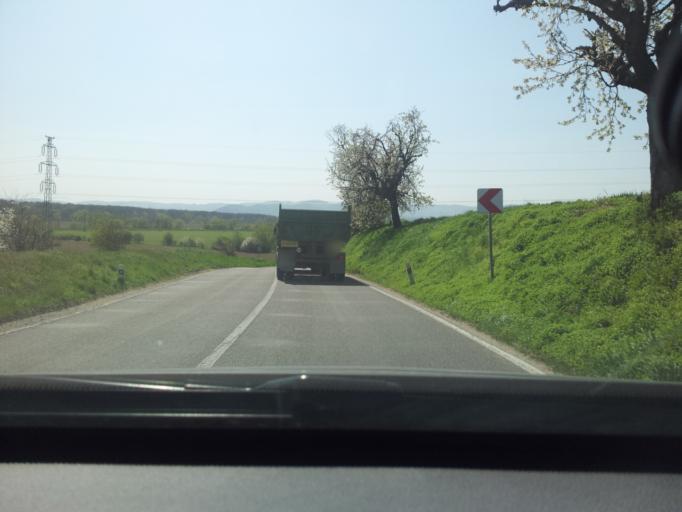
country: SK
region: Nitriansky
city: Banovce nad Bebravou
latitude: 48.6328
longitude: 18.2539
